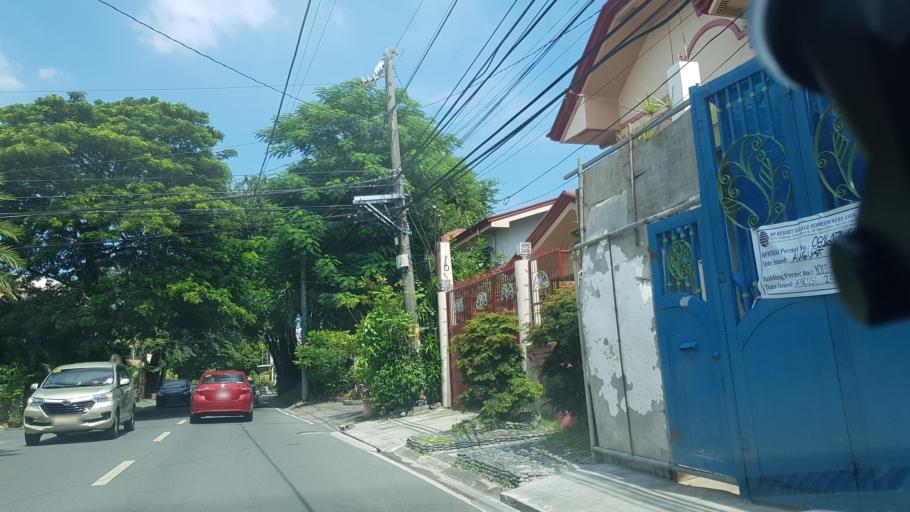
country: PH
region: Calabarzon
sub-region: Province of Rizal
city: Las Pinas
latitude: 14.4355
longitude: 120.9929
